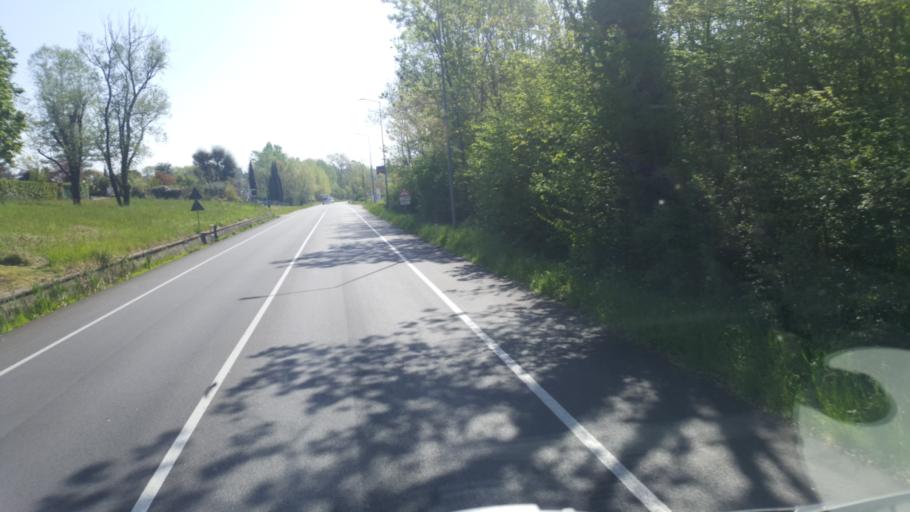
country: IT
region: Lombardy
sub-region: Provincia di Varese
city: Casciago
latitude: 45.8091
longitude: 8.7776
